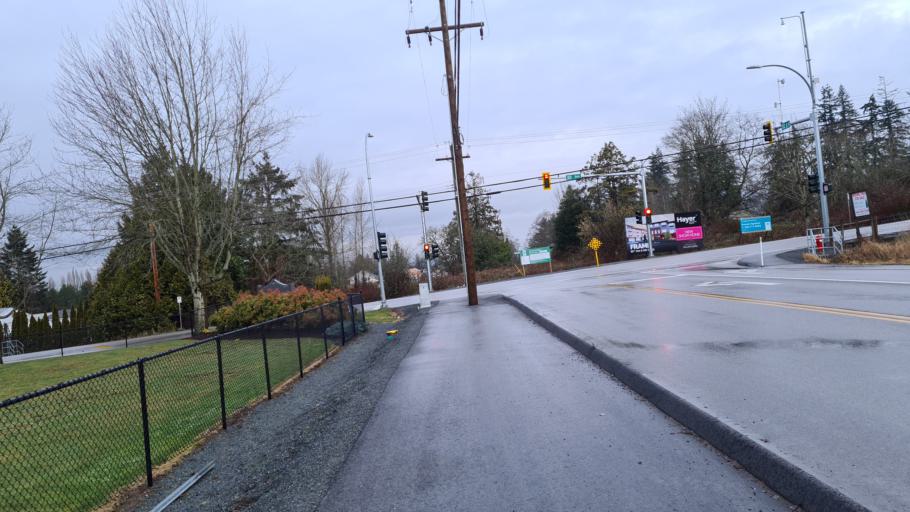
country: CA
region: British Columbia
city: Walnut Grove
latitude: 49.1478
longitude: -122.6615
